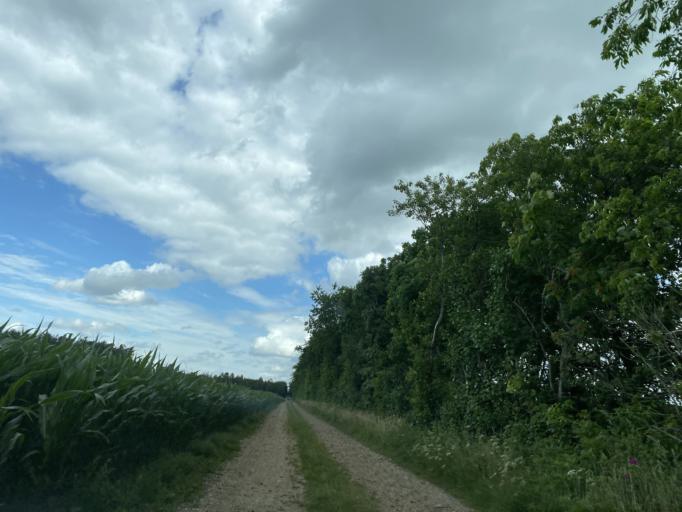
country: DK
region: Central Jutland
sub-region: Viborg Kommune
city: Bjerringbro
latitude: 56.2809
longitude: 9.6572
